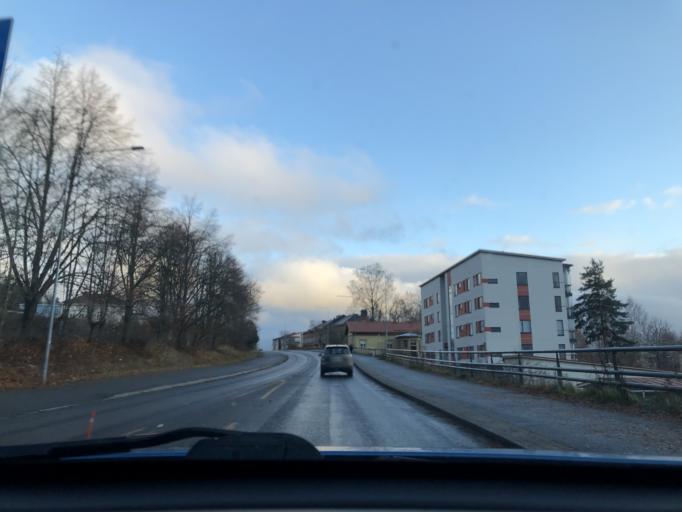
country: FI
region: Pirkanmaa
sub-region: Tampere
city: Kangasala
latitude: 61.4644
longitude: 24.0593
